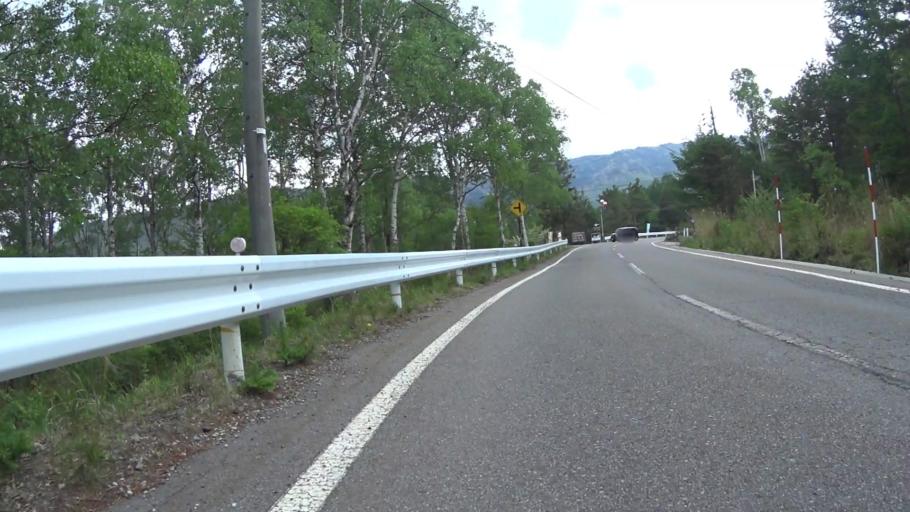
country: JP
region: Nagano
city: Saku
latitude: 36.0780
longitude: 138.3853
